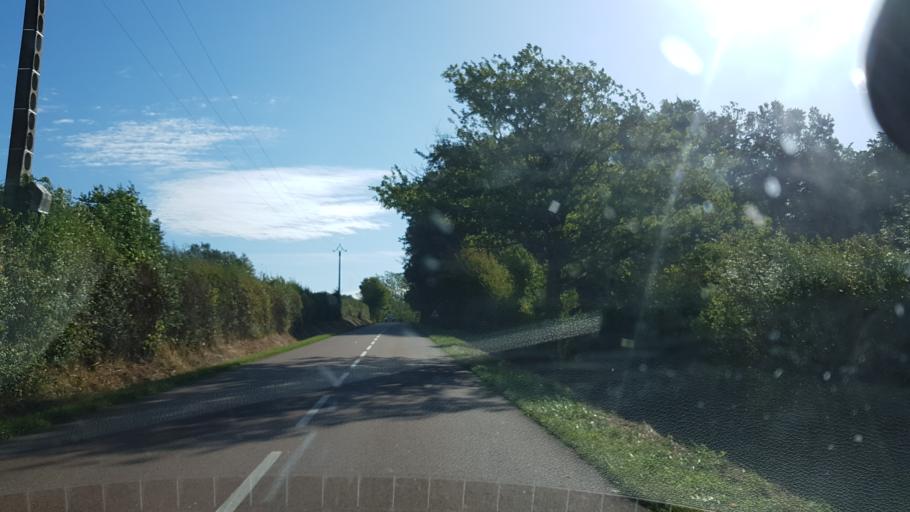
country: FR
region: Bourgogne
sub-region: Departement de la Nievre
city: Saint-Amand-en-Puisaye
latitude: 47.5372
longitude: 3.0315
